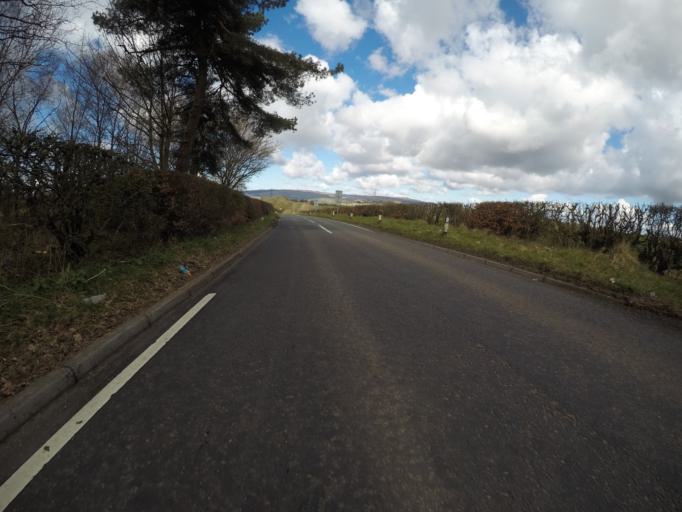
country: GB
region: Scotland
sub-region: North Ayrshire
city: Beith
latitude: 55.7381
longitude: -4.6208
